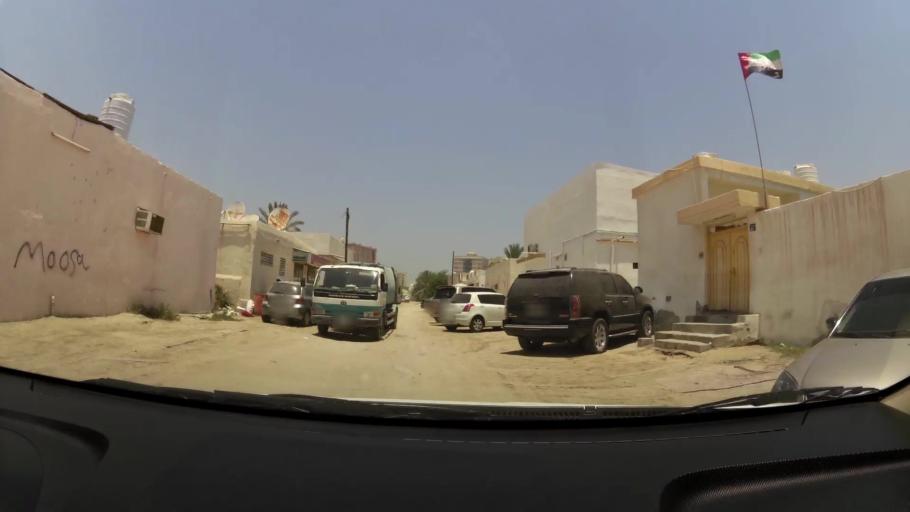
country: AE
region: Ajman
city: Ajman
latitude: 25.3965
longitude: 55.4384
